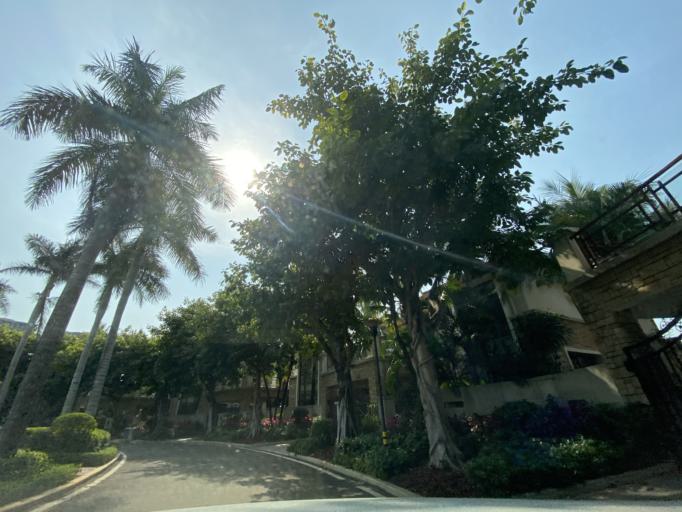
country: CN
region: Hainan
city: Yingzhou
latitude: 18.4148
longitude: 109.8430
